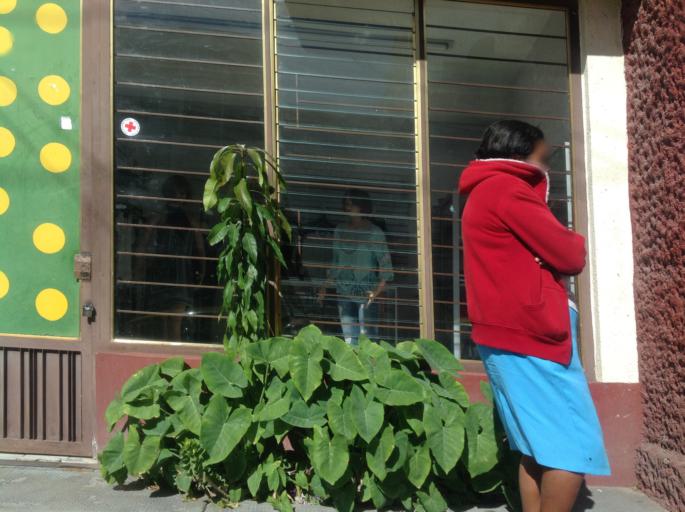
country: MX
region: Oaxaca
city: Ciudad de Huajuapam de Leon
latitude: 17.8089
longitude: -97.7743
